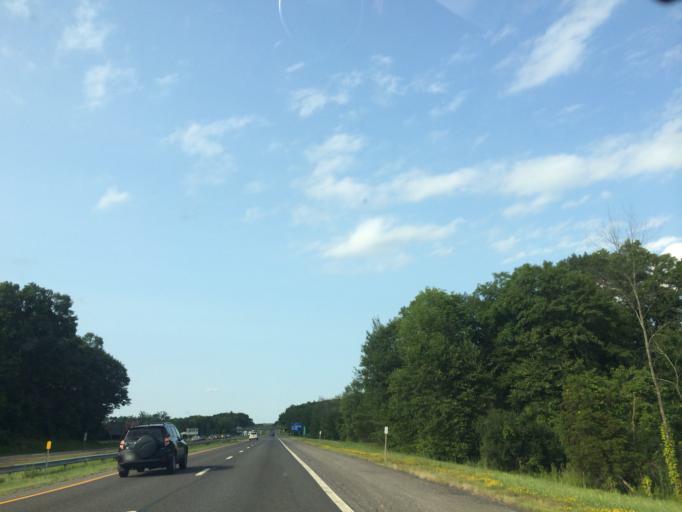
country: US
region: New York
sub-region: Ulster County
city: Saugerties
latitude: 42.0923
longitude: -73.9680
